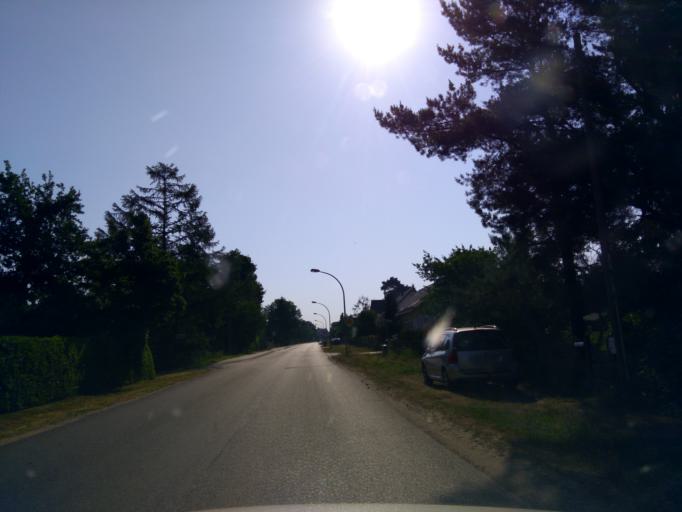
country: DE
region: Brandenburg
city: Dallgow-Doeberitz
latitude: 52.5604
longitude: 13.0291
